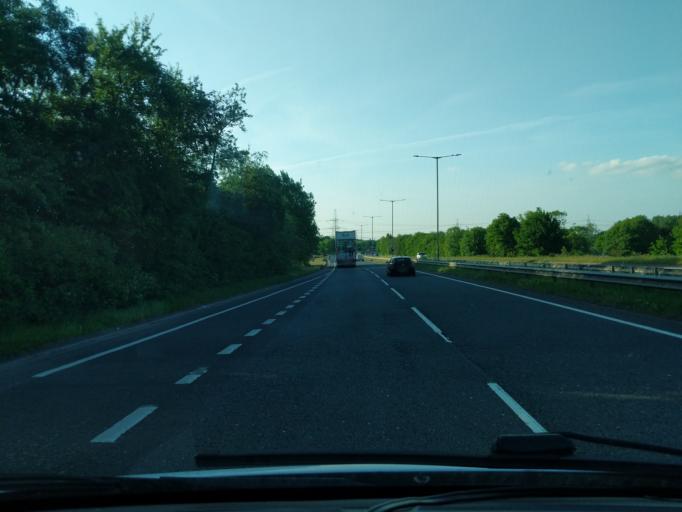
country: GB
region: England
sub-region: St. Helens
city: St Helens
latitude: 53.4123
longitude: -2.7444
